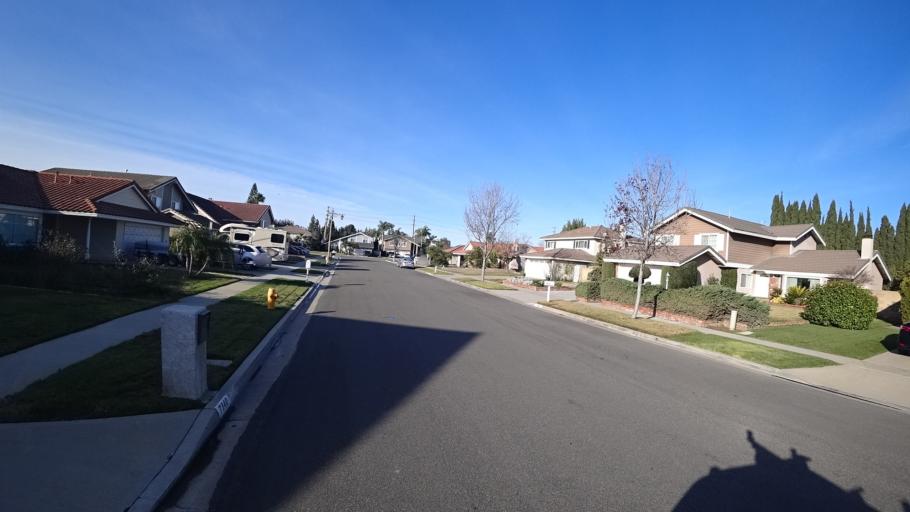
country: US
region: California
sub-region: Orange County
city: Yorba Linda
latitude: 33.8603
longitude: -117.7714
